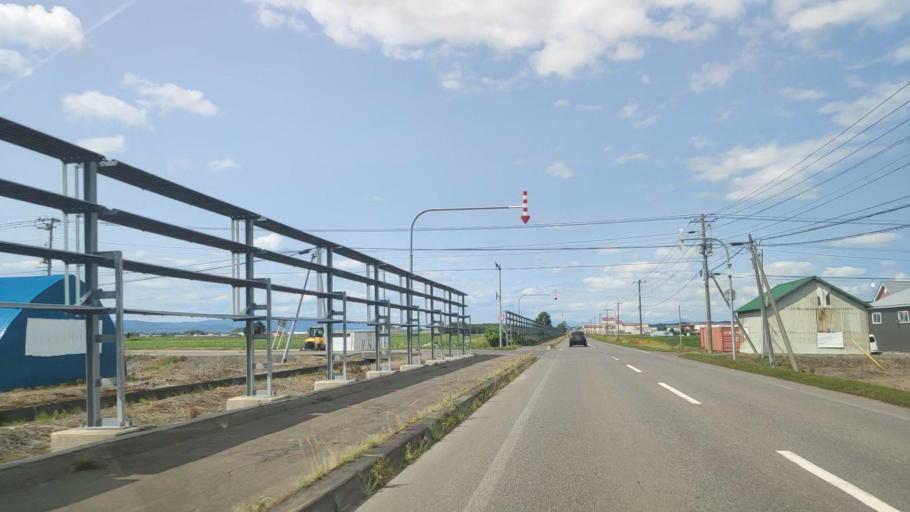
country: JP
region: Hokkaido
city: Nayoro
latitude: 44.1954
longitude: 142.4159
